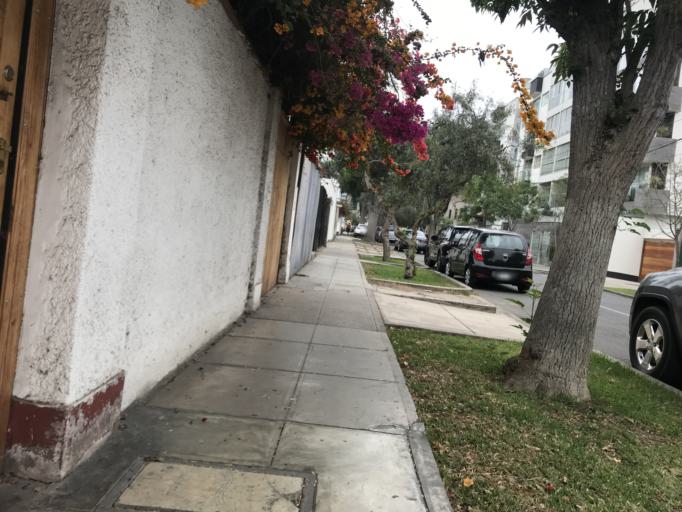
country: PE
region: Lima
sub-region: Lima
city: San Isidro
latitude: -12.0915
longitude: -77.0363
